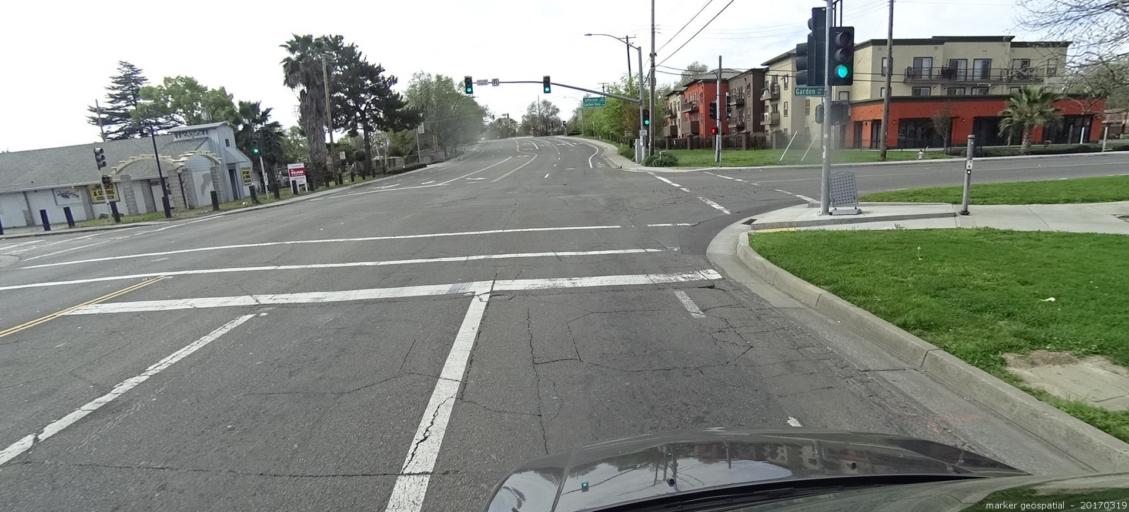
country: US
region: California
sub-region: Sacramento County
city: Sacramento
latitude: 38.6070
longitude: -121.4757
